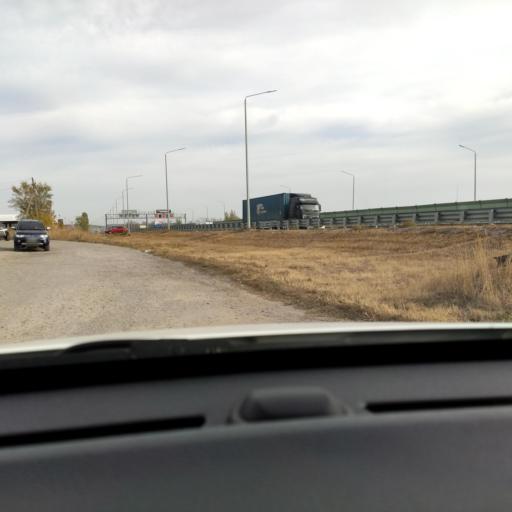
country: RU
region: Voronezj
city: Somovo
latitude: 51.6681
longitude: 39.2999
